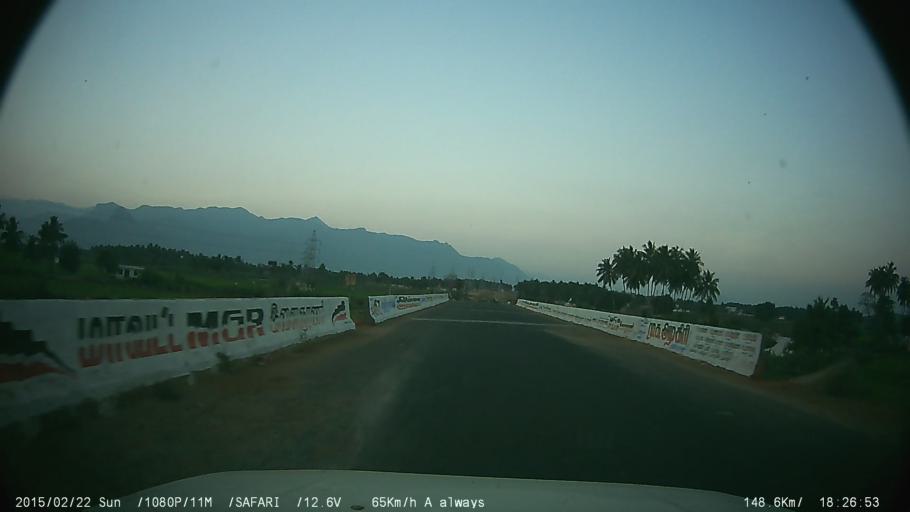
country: IN
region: Tamil Nadu
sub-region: Theni
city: Teni
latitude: 9.9673
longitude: 77.4406
